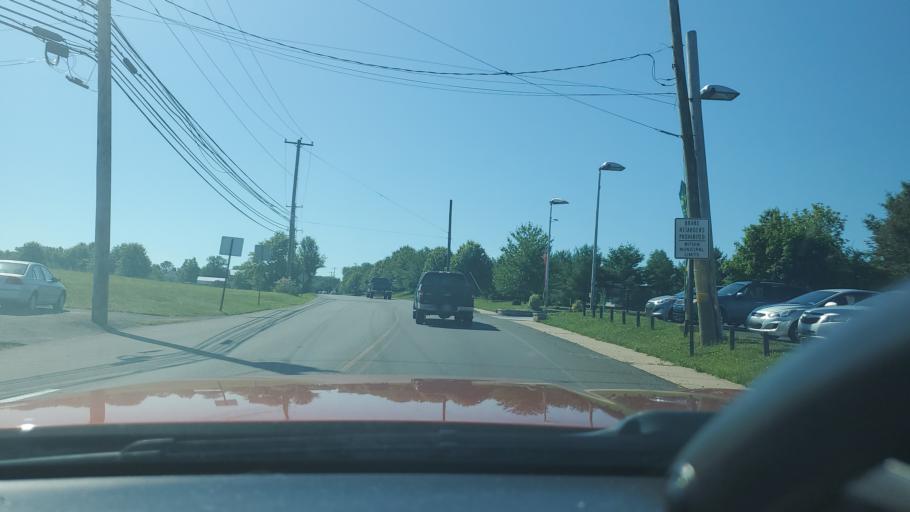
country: US
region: Pennsylvania
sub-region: Montgomery County
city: Limerick
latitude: 40.2470
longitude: -75.5341
